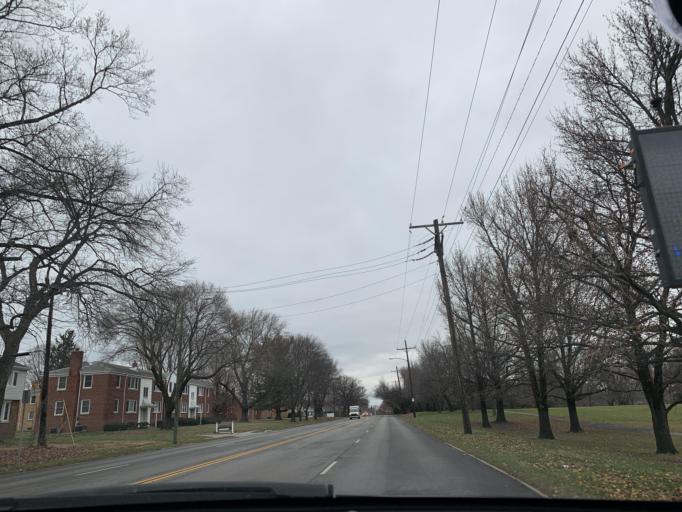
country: US
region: Illinois
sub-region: Sangamon County
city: Leland Grove
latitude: 39.7910
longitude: -89.6869
